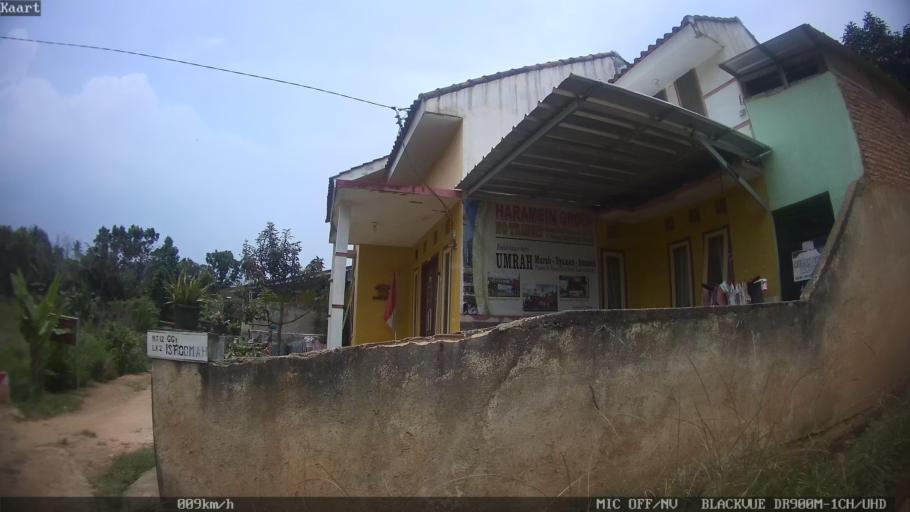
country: ID
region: Lampung
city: Kedaton
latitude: -5.3973
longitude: 105.3263
